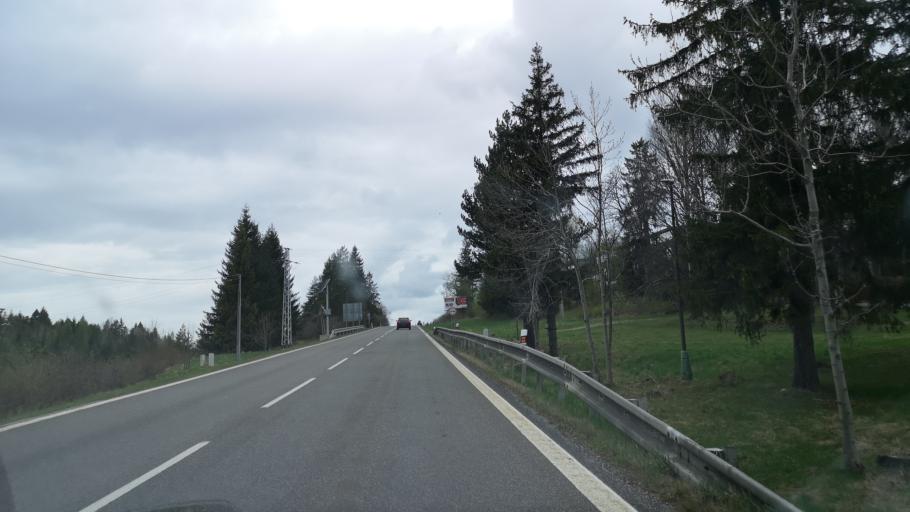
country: SK
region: Presovsky
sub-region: Okres Poprad
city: Strba
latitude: 49.0846
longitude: 20.0666
